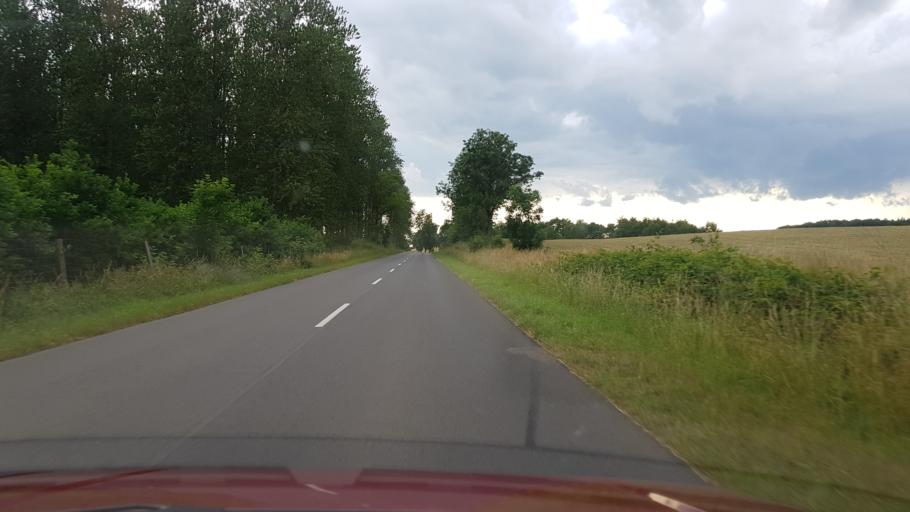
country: PL
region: West Pomeranian Voivodeship
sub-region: Powiat gryficki
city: Gryfice
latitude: 53.8817
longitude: 15.1495
